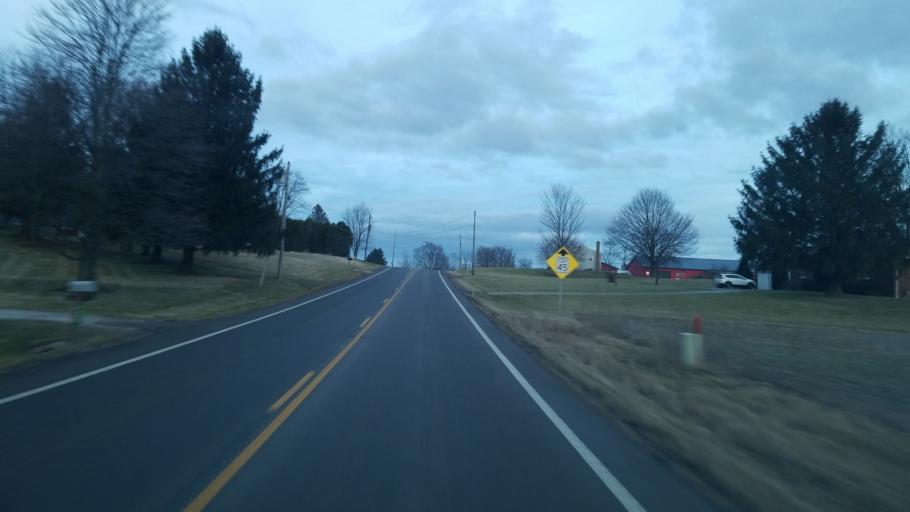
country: US
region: Ohio
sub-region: Knox County
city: Fredericktown
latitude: 40.4767
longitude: -82.5674
